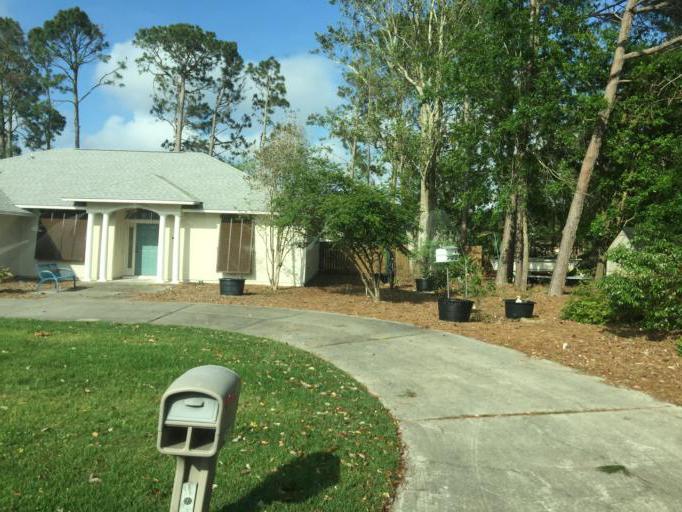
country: US
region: Florida
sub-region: Bay County
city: Panama City Beach
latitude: 30.2125
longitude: -85.8415
